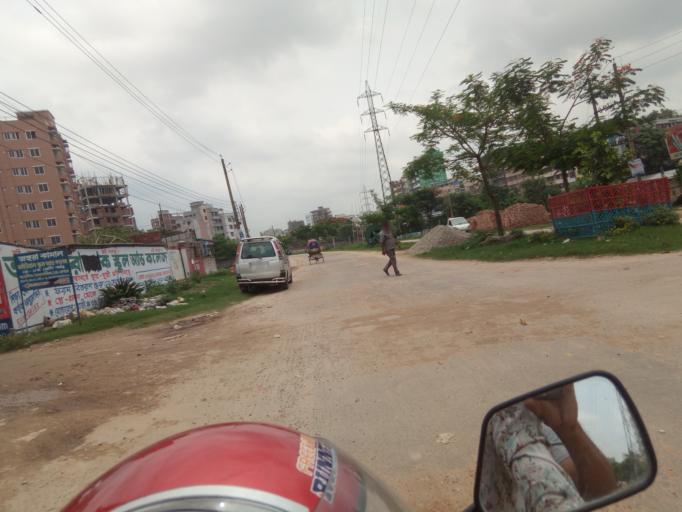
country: BD
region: Dhaka
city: Paltan
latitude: 23.7643
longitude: 90.4329
